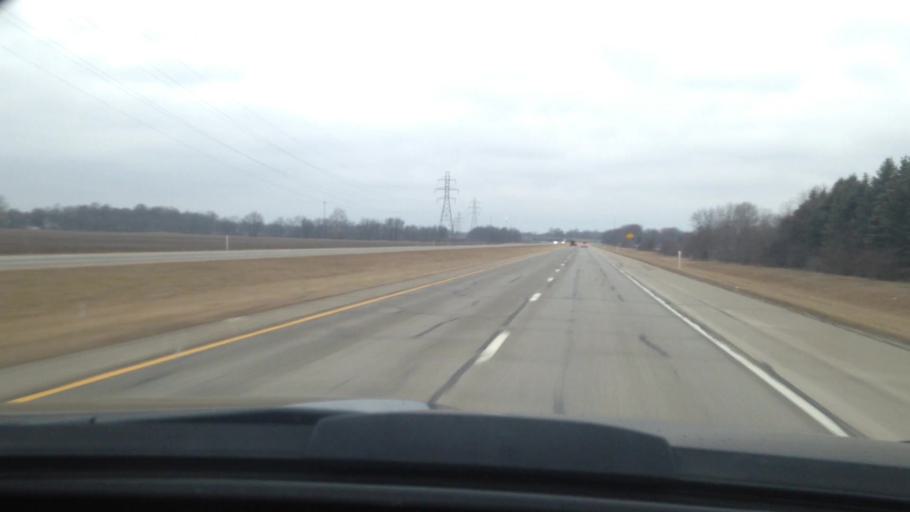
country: US
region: Indiana
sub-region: Delaware County
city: Muncie
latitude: 40.1425
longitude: -85.4155
